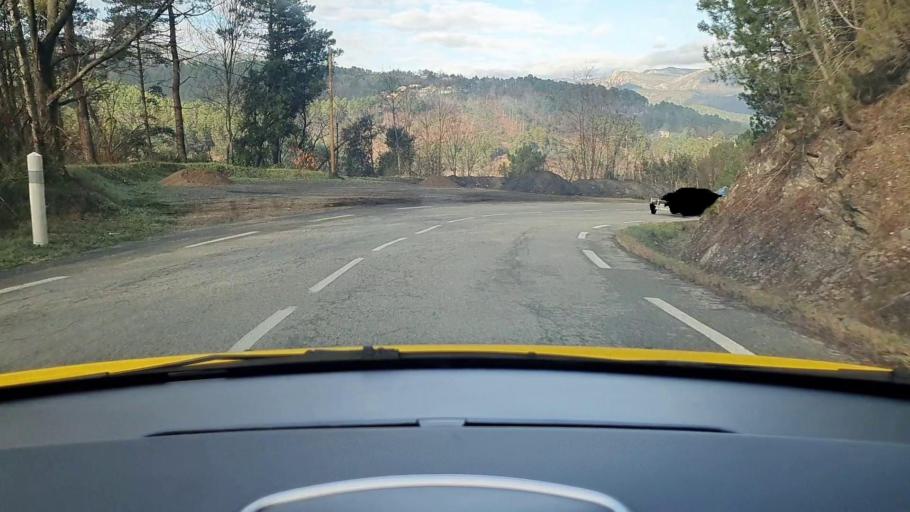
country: FR
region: Languedoc-Roussillon
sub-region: Departement du Gard
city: Branoux-les-Taillades
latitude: 44.2928
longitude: 3.9803
